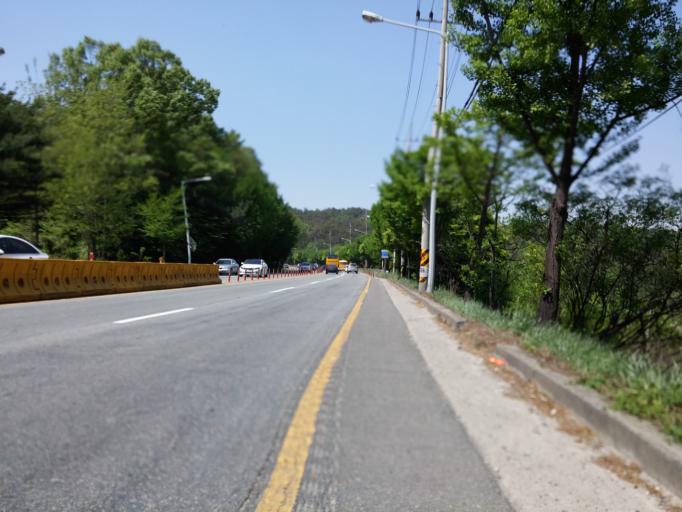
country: KR
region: Daejeon
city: Daejeon
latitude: 36.2797
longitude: 127.2987
